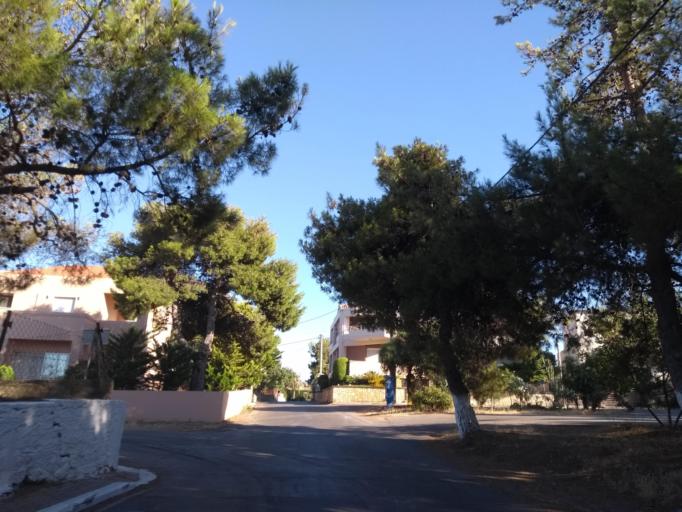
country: GR
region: Crete
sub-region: Nomos Chanias
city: Pithari
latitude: 35.5218
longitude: 24.0776
